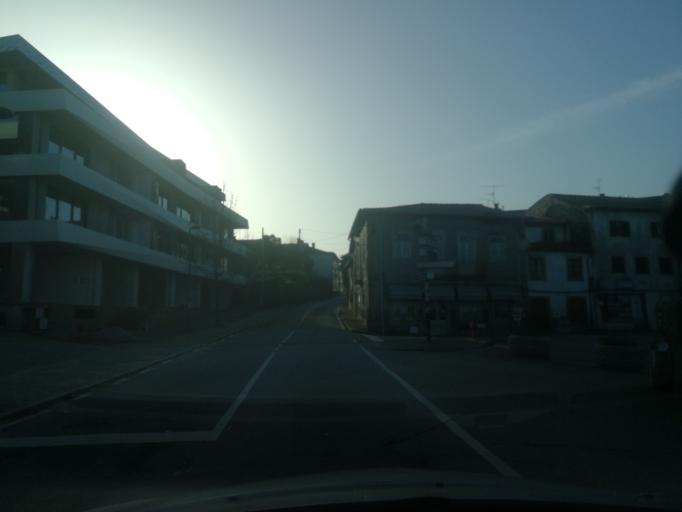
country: PT
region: Braga
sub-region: Barcelos
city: Barcelos
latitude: 41.5260
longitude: -8.6204
